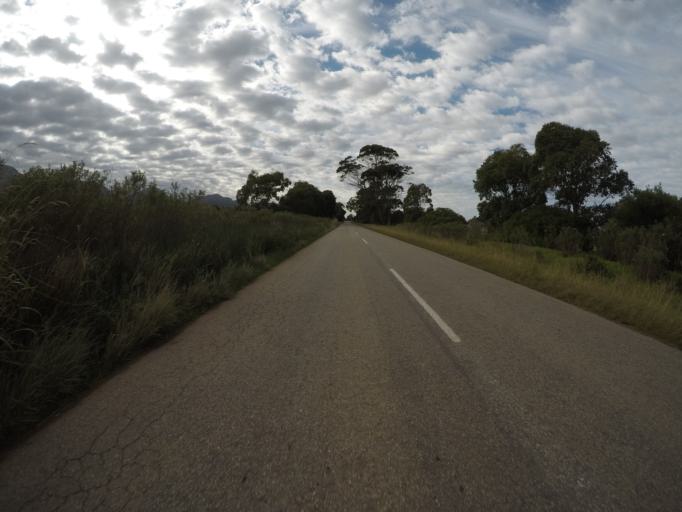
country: ZA
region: Eastern Cape
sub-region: Cacadu District Municipality
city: Kareedouw
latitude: -34.0441
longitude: 24.4325
